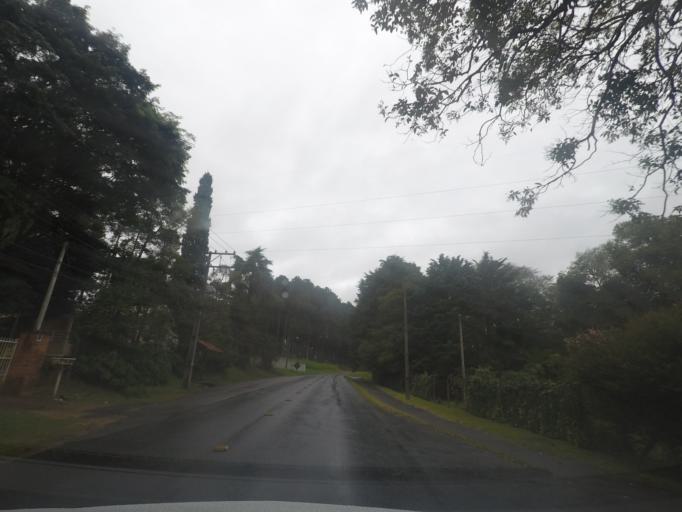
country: BR
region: Parana
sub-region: Quatro Barras
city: Quatro Barras
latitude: -25.3833
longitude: -49.1349
